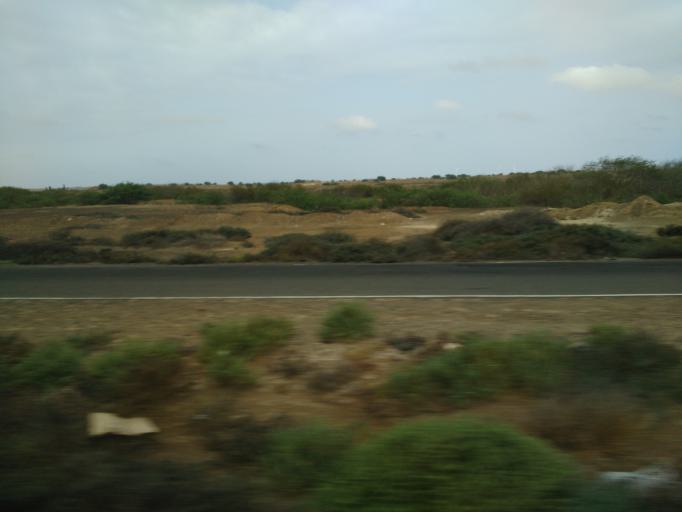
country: CV
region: Sal
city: Espargos
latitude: 16.6914
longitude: -22.9405
